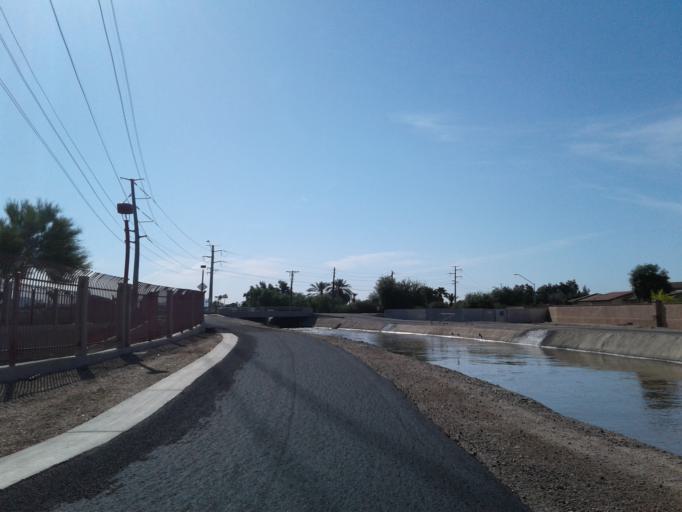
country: US
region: Arizona
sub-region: Maricopa County
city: Glendale
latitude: 33.5960
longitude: -112.1698
